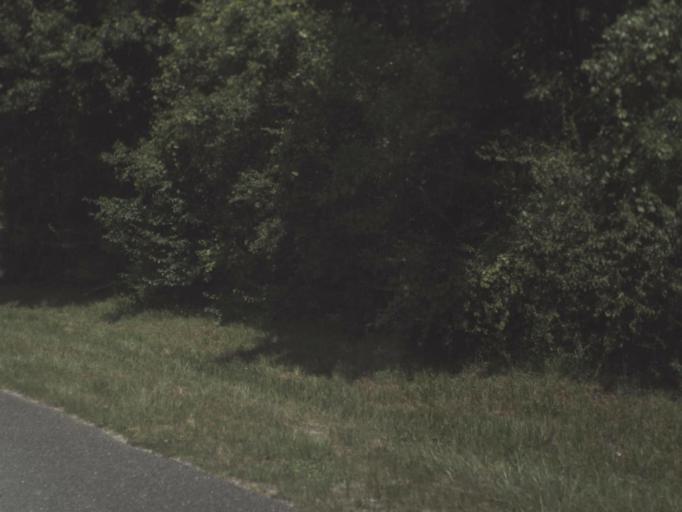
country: US
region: Florida
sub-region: Columbia County
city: Lake City
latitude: 30.1527
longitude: -82.6933
